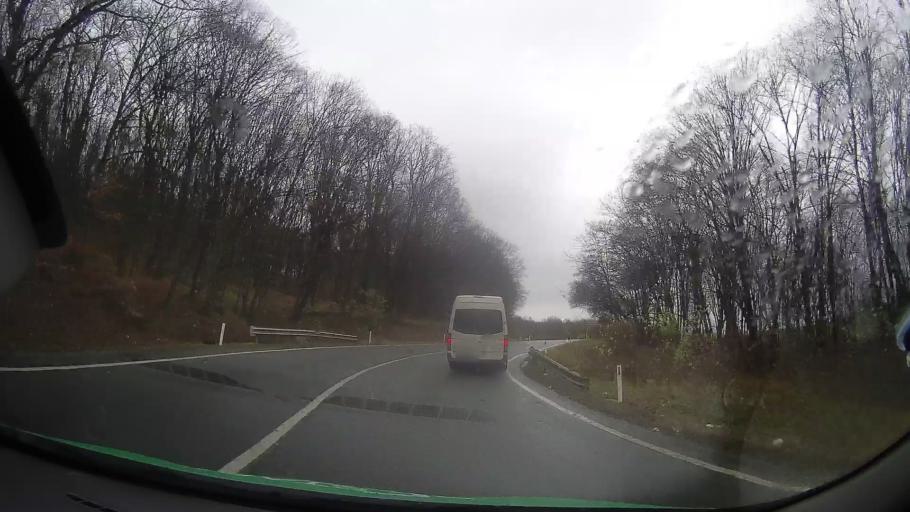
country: RO
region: Bistrita-Nasaud
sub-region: Comuna Sieu-Magherus
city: Sieu-Magherus
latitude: 47.0411
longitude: 24.4202
